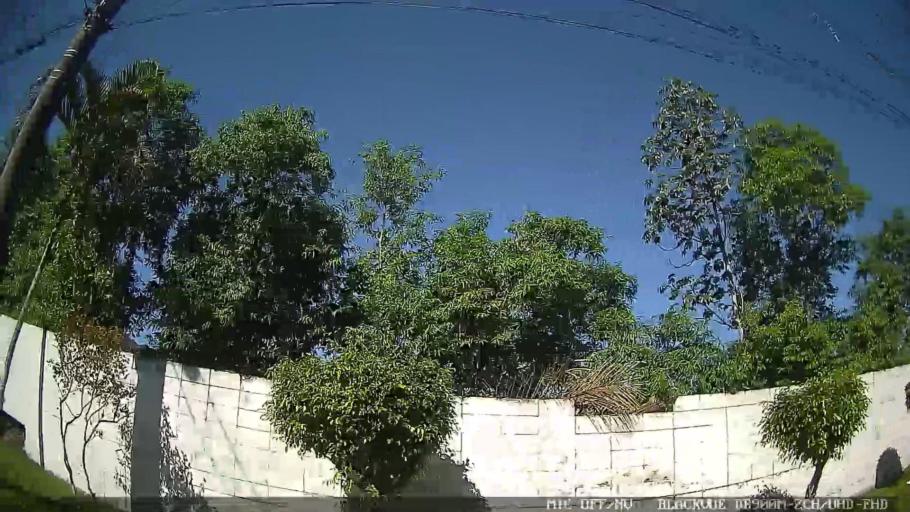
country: BR
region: Sao Paulo
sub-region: Guaruja
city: Guaruja
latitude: -23.9876
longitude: -46.2015
